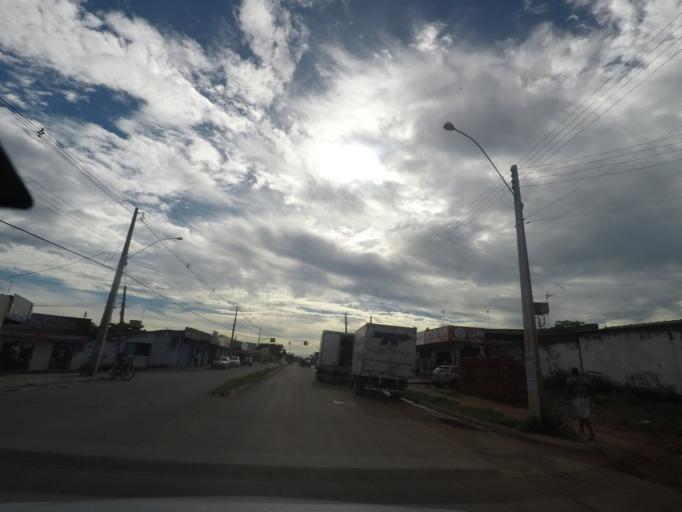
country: BR
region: Goias
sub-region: Aparecida De Goiania
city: Aparecida de Goiania
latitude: -16.8161
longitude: -49.3141
